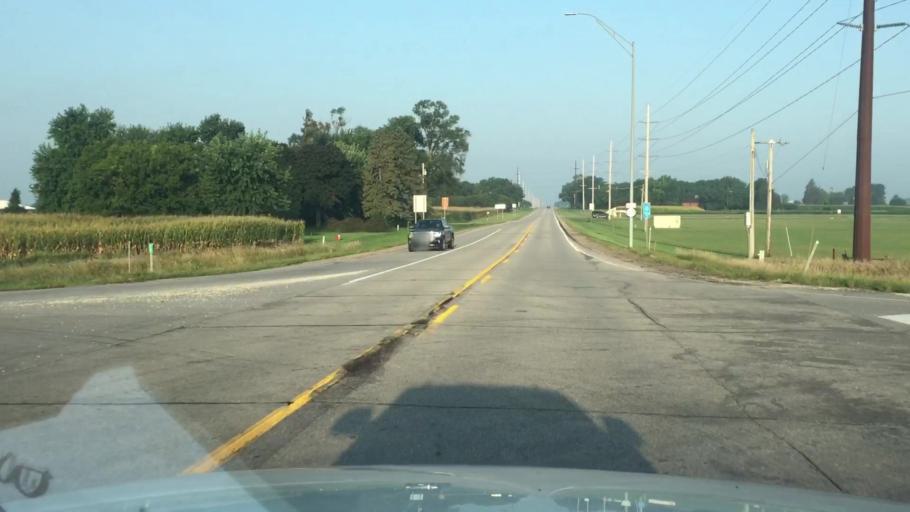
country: US
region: Iowa
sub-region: Story County
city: Huxley
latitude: 41.8778
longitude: -93.5733
